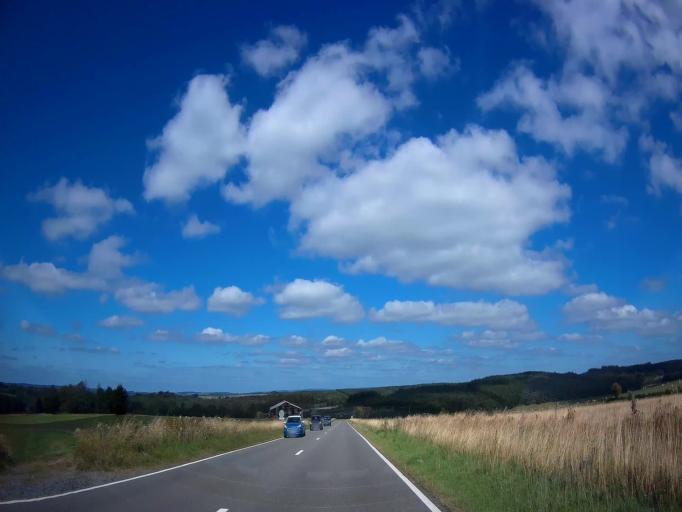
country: BE
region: Wallonia
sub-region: Province du Luxembourg
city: Bastogne
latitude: 50.0243
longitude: 5.7045
